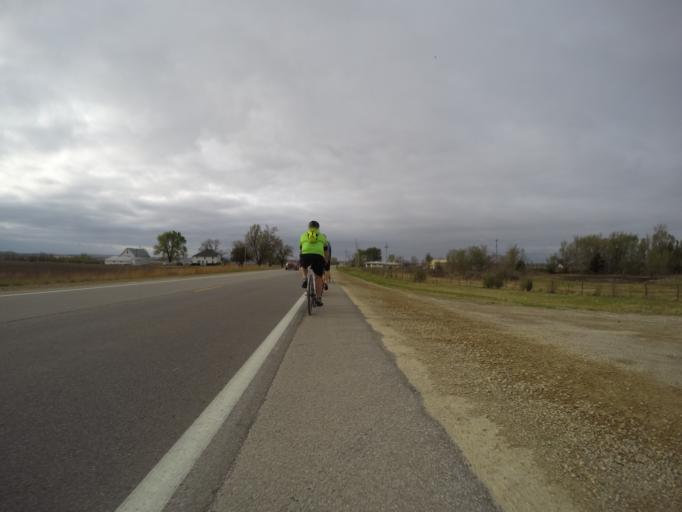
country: US
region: Kansas
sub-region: Pottawatomie County
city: Wamego
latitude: 39.1932
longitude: -96.3053
